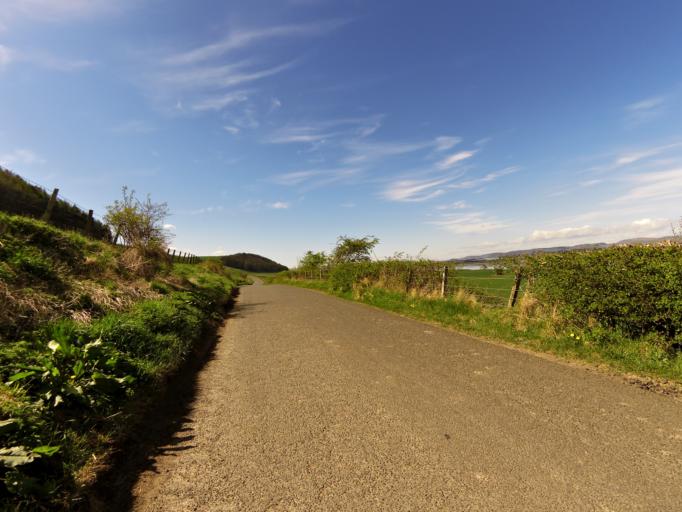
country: GB
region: Scotland
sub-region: Perth and Kinross
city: Errol
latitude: 56.3728
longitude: -3.1571
